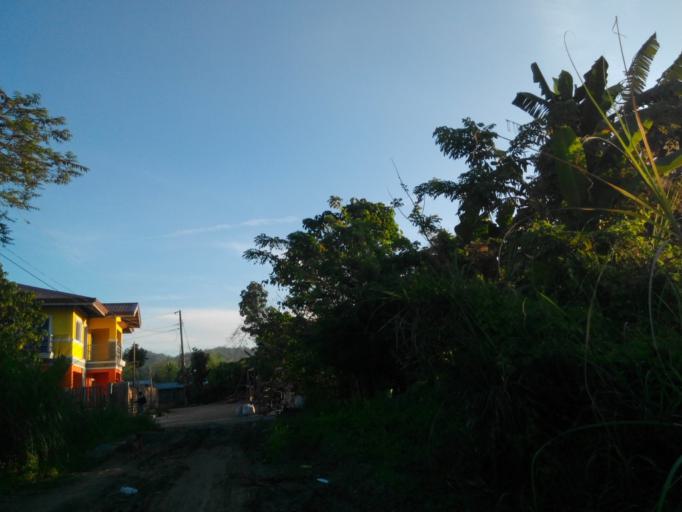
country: PH
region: Western Visayas
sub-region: Province of Iloilo
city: Passi
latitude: 11.1221
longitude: 122.6494
